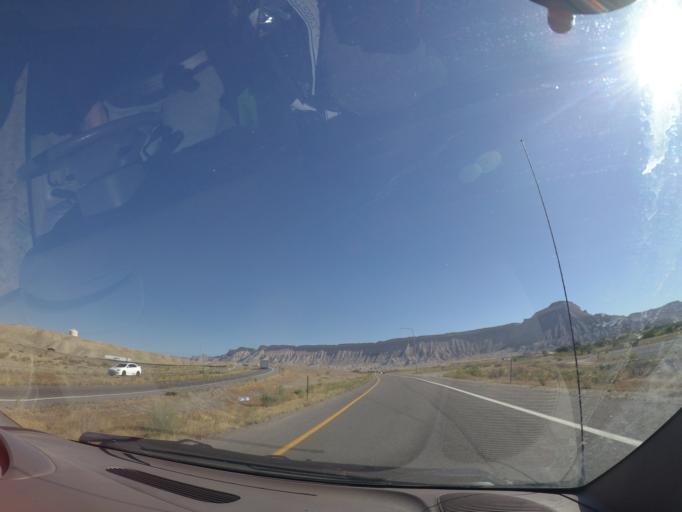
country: US
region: Colorado
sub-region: Mesa County
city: Clifton
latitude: 39.1013
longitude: -108.4471
